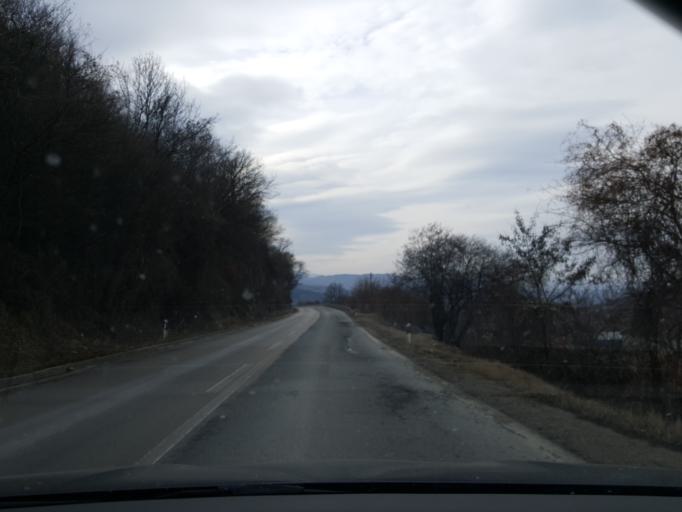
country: RS
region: Central Serbia
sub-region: Pirotski Okrug
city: Dimitrovgrad
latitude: 43.0108
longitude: 22.7681
